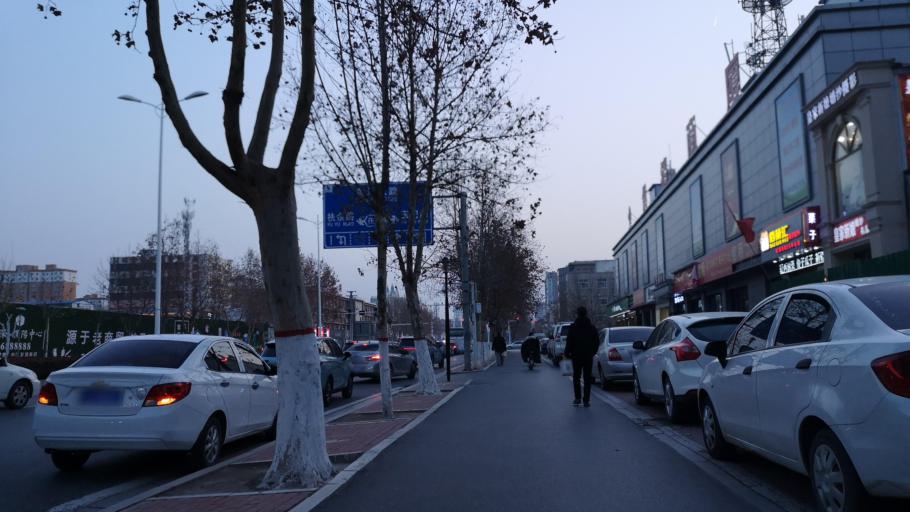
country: CN
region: Henan Sheng
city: Zhongyuanlu
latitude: 35.7743
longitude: 115.0701
